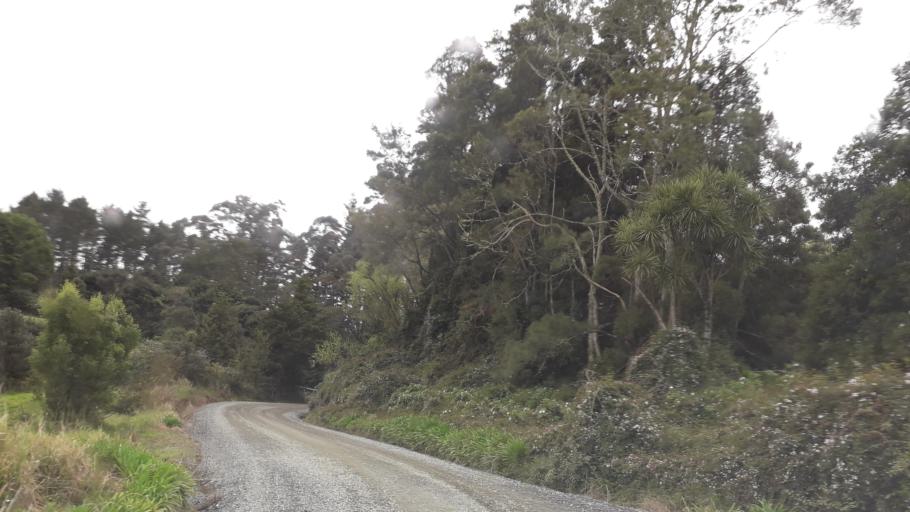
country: NZ
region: Northland
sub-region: Far North District
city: Kerikeri
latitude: -35.1202
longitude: 173.7516
